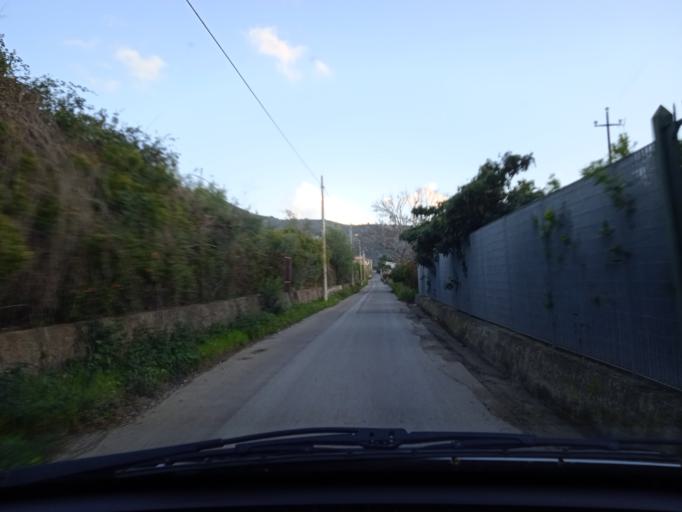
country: IT
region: Sicily
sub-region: Palermo
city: Villabate
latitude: 38.0819
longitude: 13.4259
